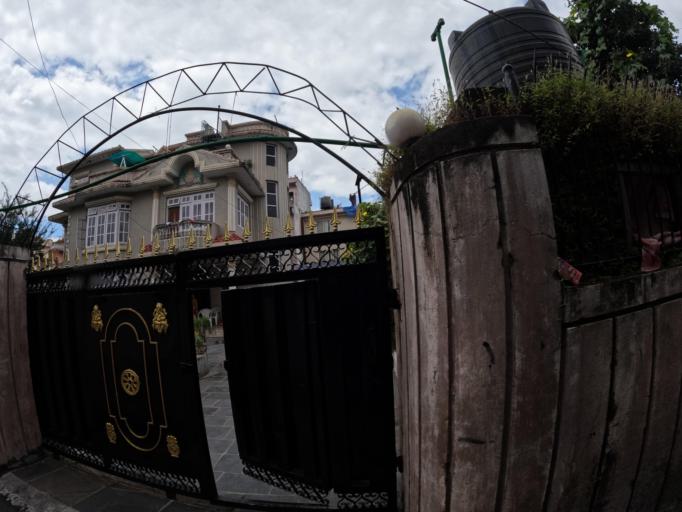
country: NP
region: Central Region
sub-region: Bagmati Zone
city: Kathmandu
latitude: 27.7425
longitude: 85.3184
